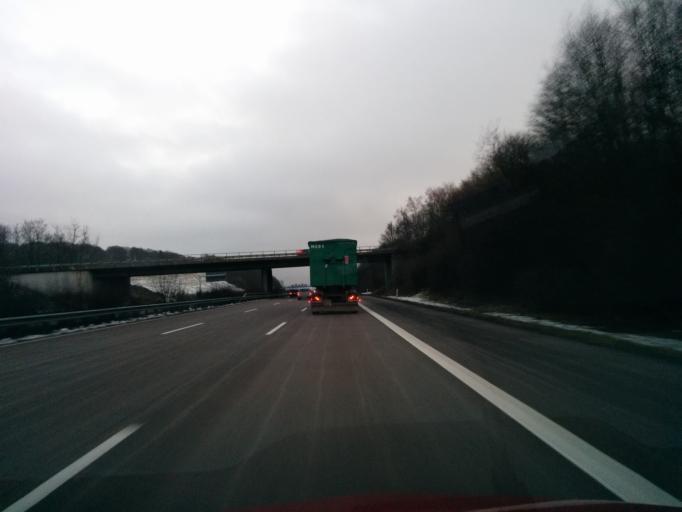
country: DE
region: Rheinland-Pfalz
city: Wehr
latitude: 50.4099
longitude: 7.2365
